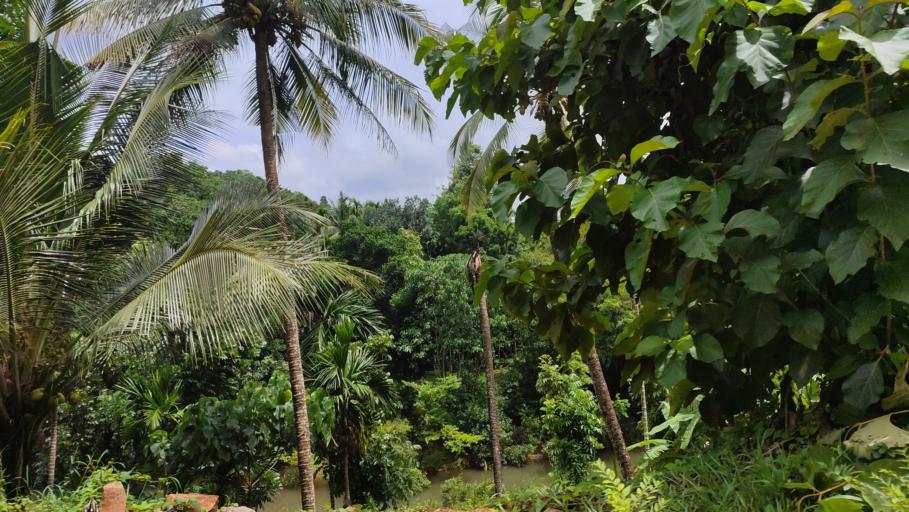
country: IN
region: Kerala
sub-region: Kasaragod District
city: Nileshwar
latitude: 12.2957
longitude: 75.2776
